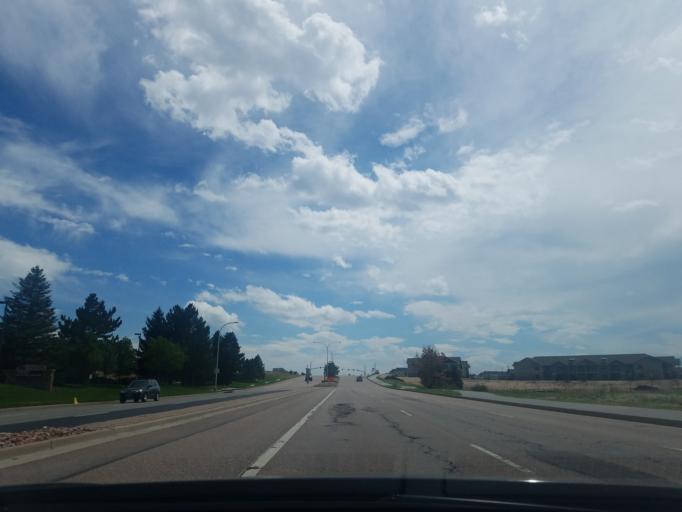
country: US
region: Colorado
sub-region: El Paso County
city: Gleneagle
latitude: 38.9981
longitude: -104.7980
